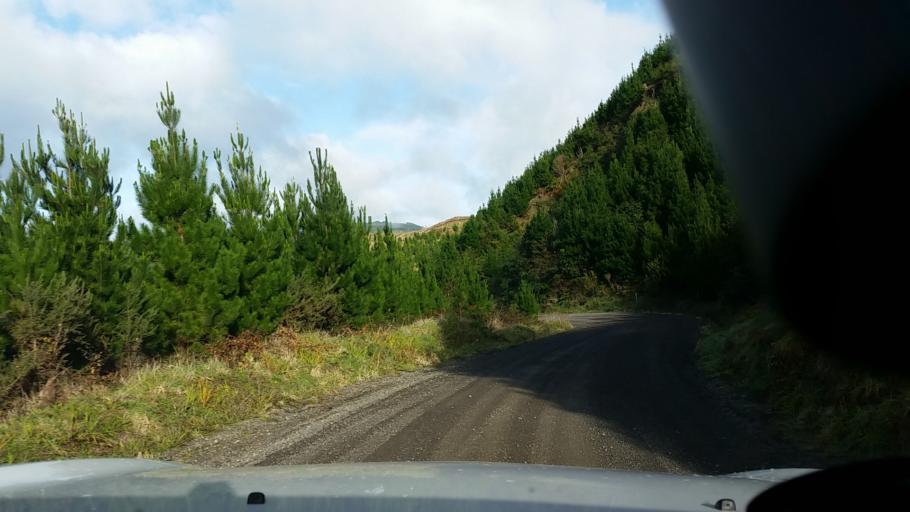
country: NZ
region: Bay of Plenty
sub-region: Kawerau District
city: Kawerau
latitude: -38.0318
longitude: 176.5540
